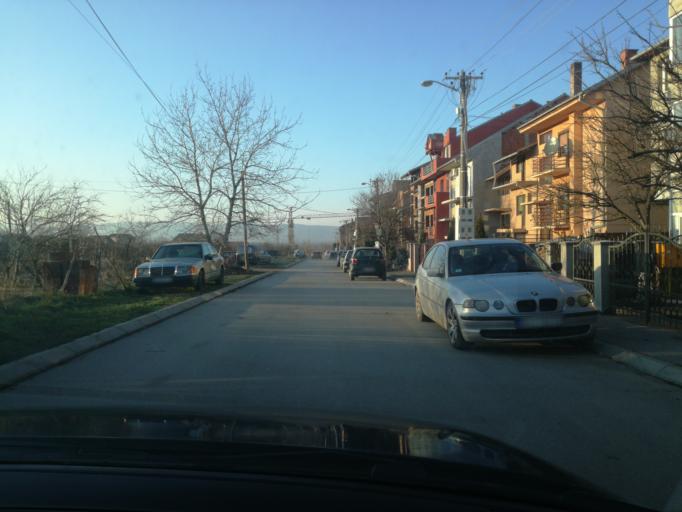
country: RS
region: Central Serbia
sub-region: Nisavski Okrug
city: Nis
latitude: 43.3089
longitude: 21.8602
